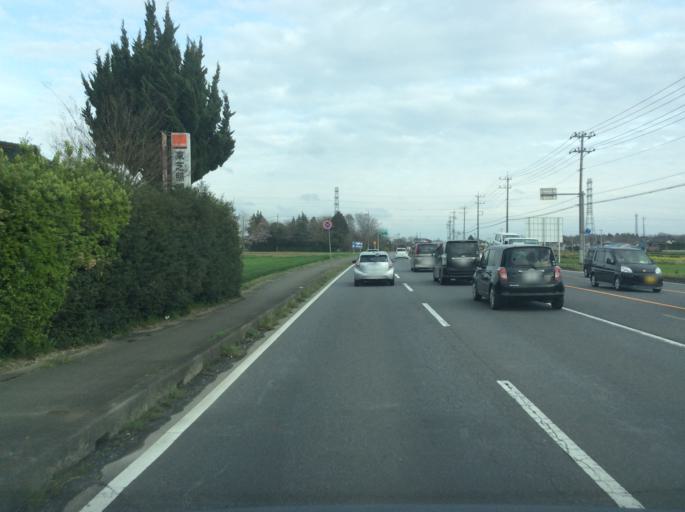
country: JP
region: Ibaraki
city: Naka
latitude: 36.1285
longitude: 140.1664
